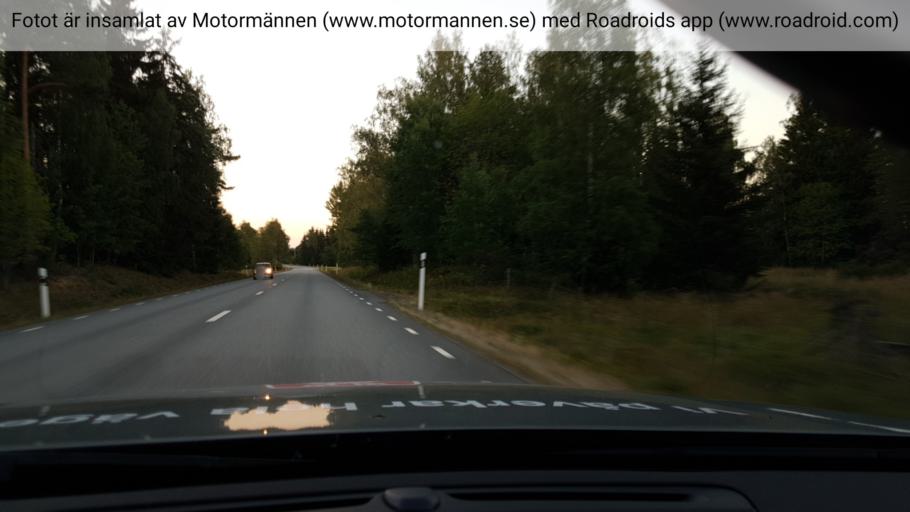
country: SE
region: Uppsala
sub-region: Heby Kommun
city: OEstervala
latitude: 60.1526
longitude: 17.2017
